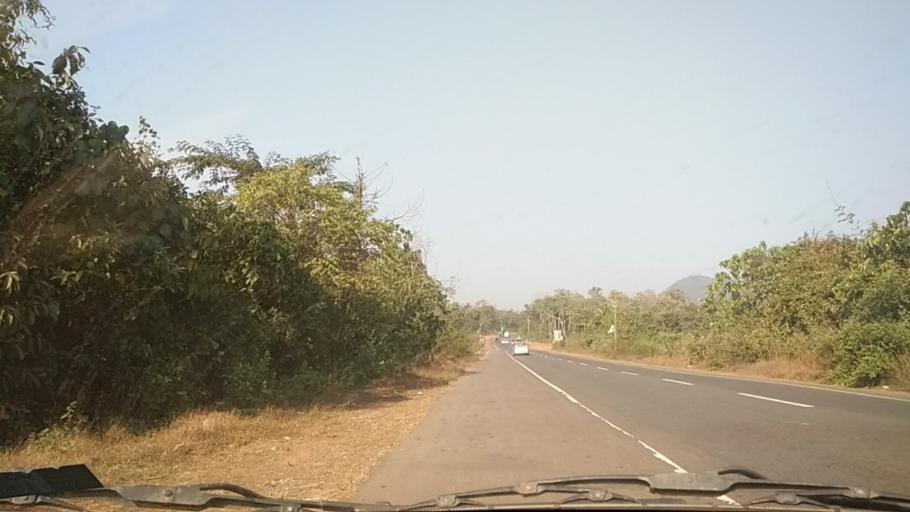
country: IN
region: Goa
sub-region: North Goa
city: Palle
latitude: 15.3893
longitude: 74.1268
